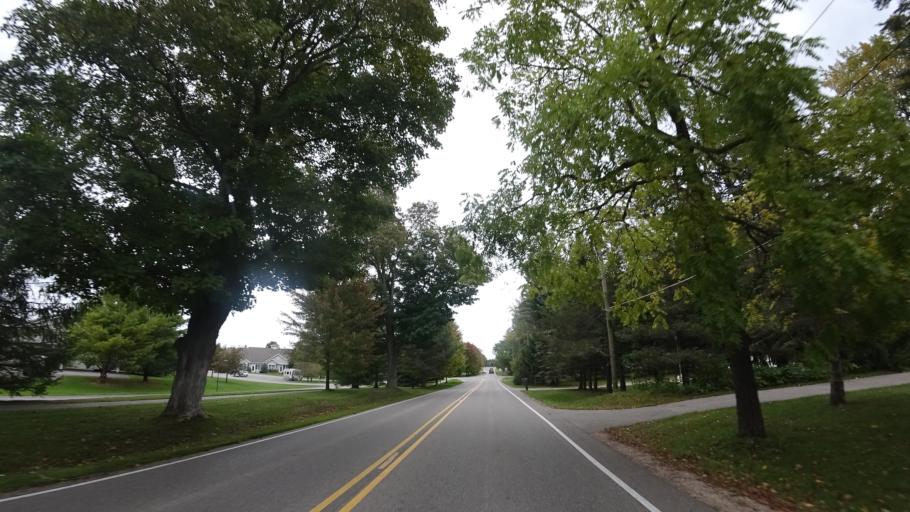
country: US
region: Michigan
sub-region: Emmet County
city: Harbor Springs
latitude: 45.4352
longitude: -85.0001
